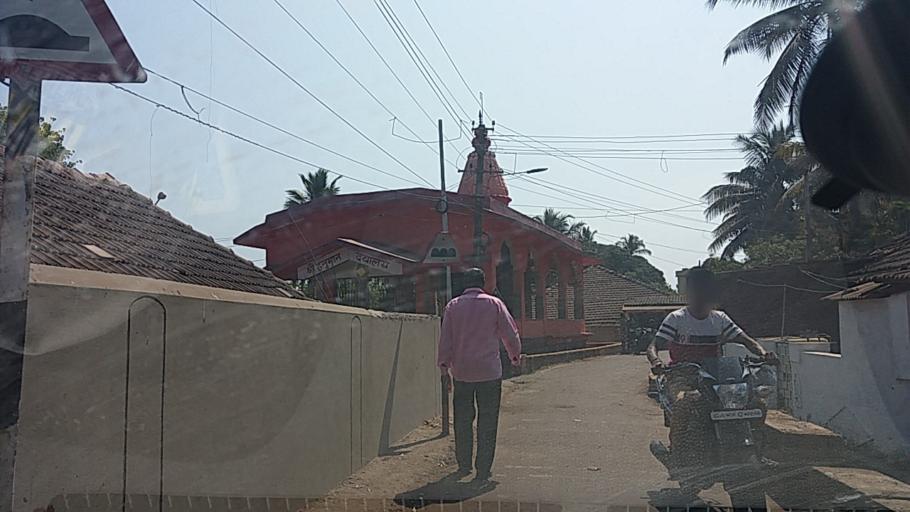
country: IN
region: Goa
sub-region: South Goa
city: Marmagao
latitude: 15.4075
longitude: 73.7922
